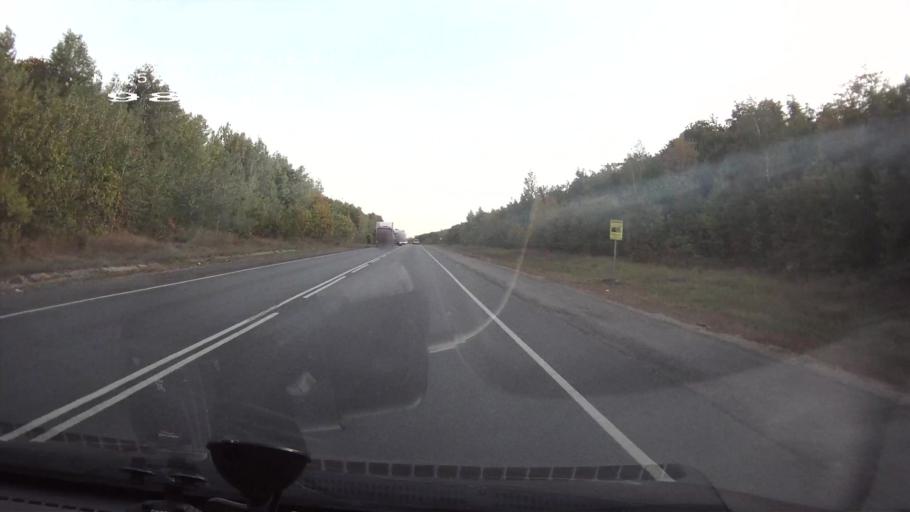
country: RU
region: Saratov
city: Sokolovyy
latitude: 51.5747
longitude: 45.7643
